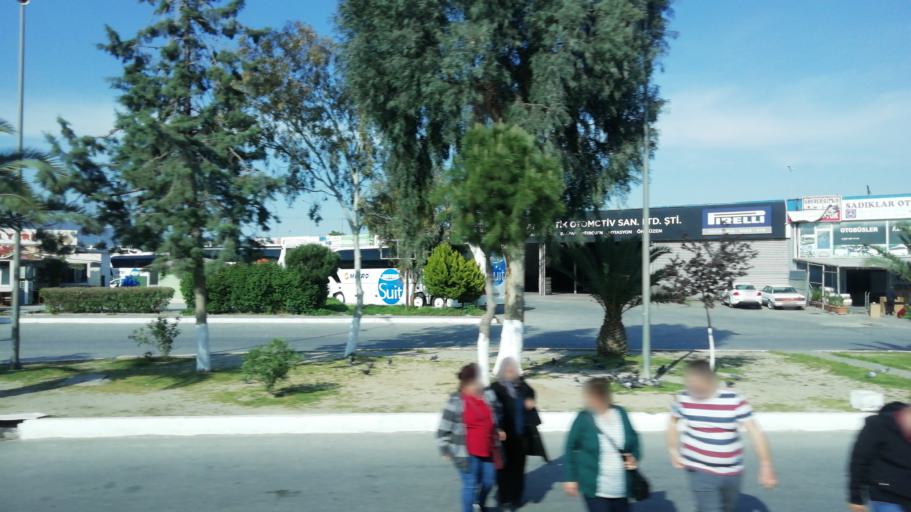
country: TR
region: Izmir
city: Bornova
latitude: 38.4316
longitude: 27.2149
